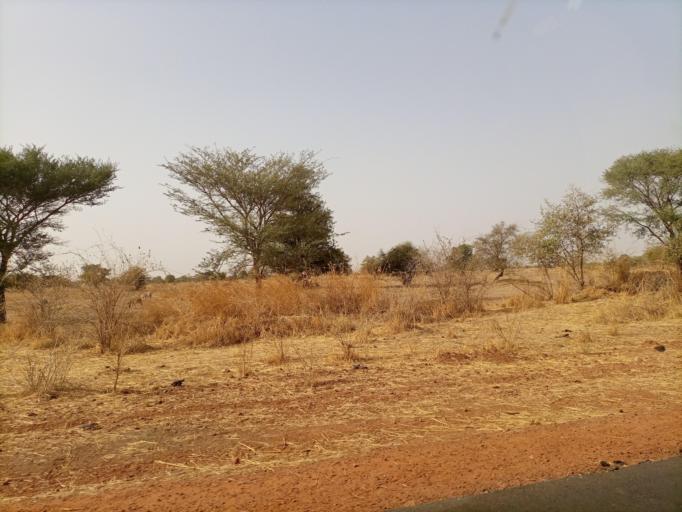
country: SN
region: Fatick
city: Foundiougne
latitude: 14.1264
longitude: -16.4178
